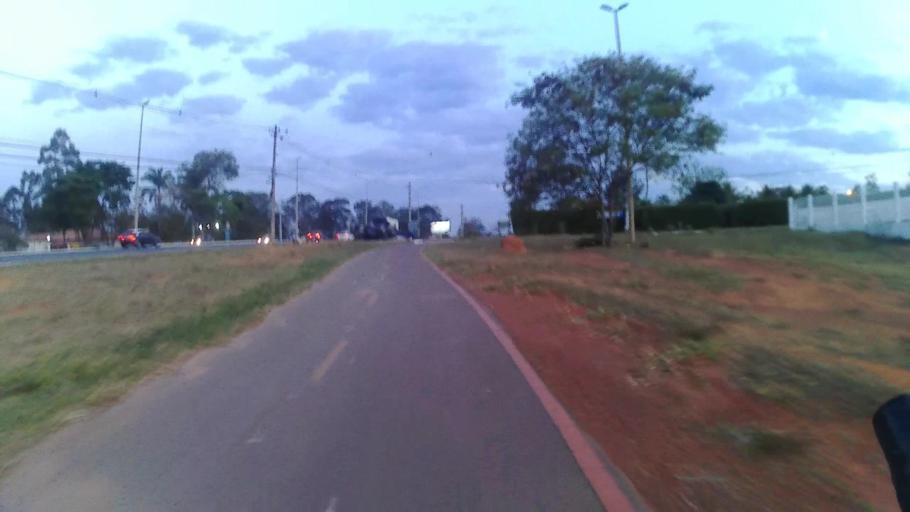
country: BR
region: Federal District
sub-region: Brasilia
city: Brasilia
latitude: -15.8627
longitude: -47.9847
